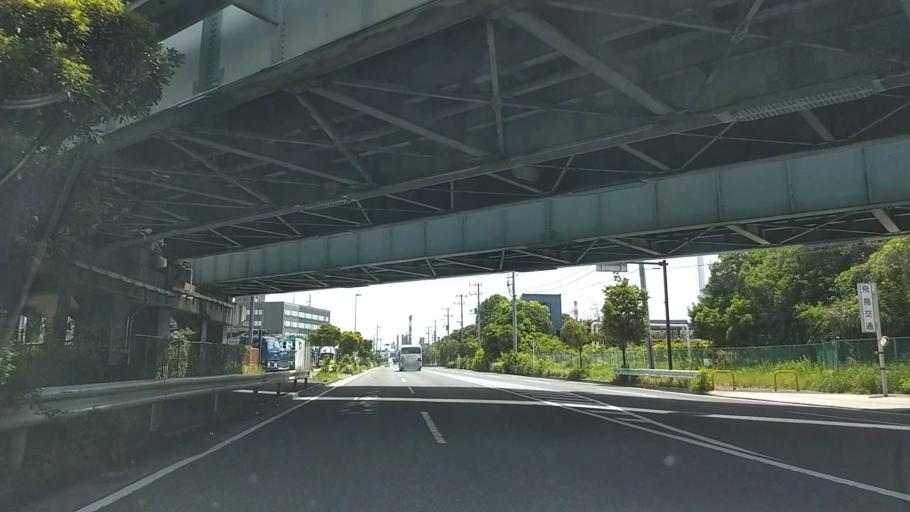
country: JP
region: Kanagawa
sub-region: Kawasaki-shi
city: Kawasaki
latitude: 35.5203
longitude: 139.7330
